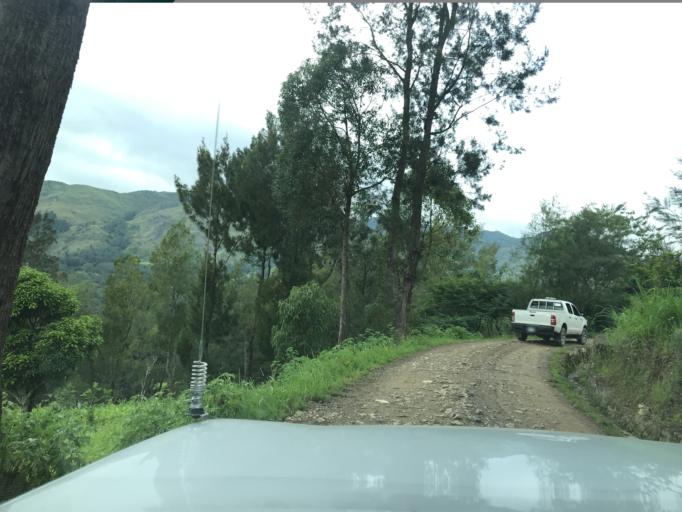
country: TL
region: Aileu
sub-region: Aileu Villa
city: Aileu
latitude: -8.8525
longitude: 125.5851
